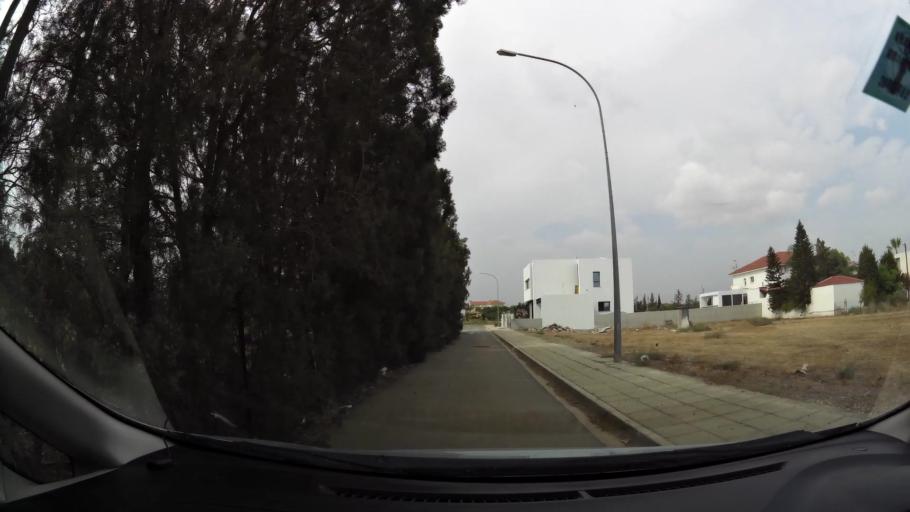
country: CY
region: Lefkosia
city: Geri
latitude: 35.0812
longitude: 33.3921
